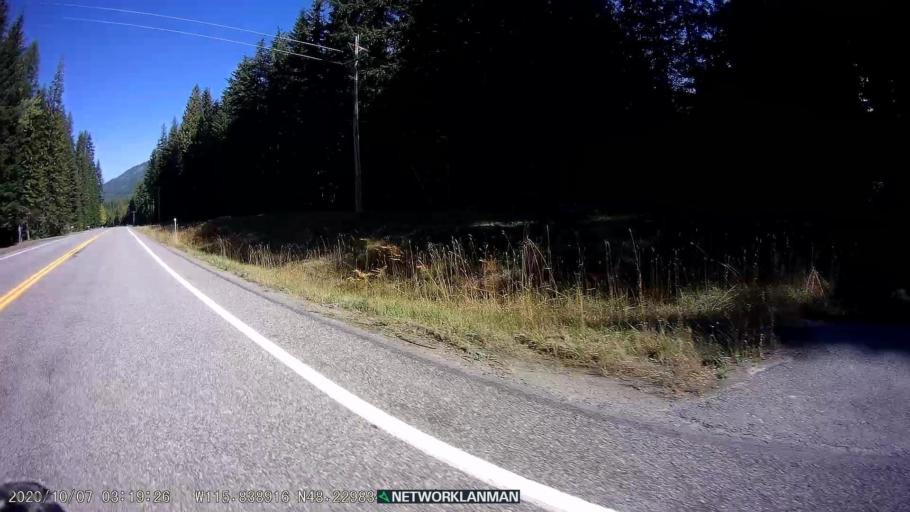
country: US
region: Montana
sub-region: Lincoln County
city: Libby
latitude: 48.2301
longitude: -115.8388
